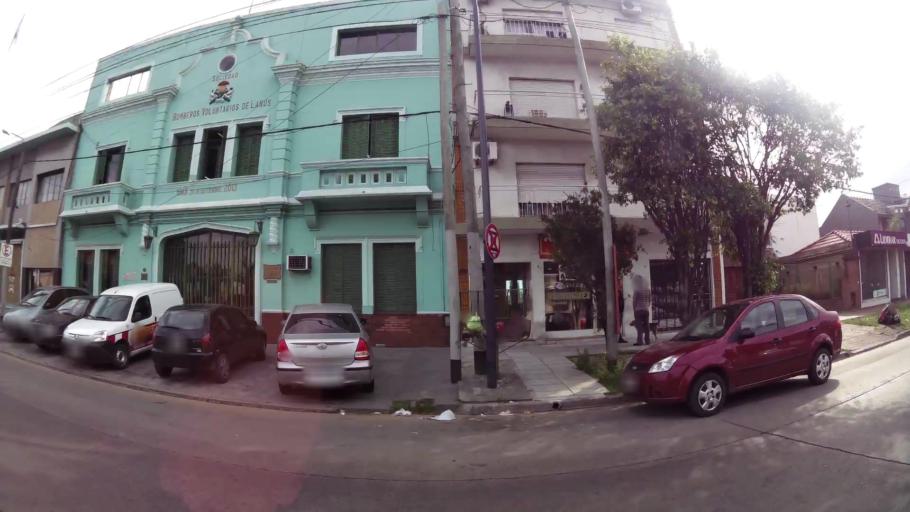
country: AR
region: Buenos Aires
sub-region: Partido de Lanus
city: Lanus
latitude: -34.6984
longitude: -58.3810
